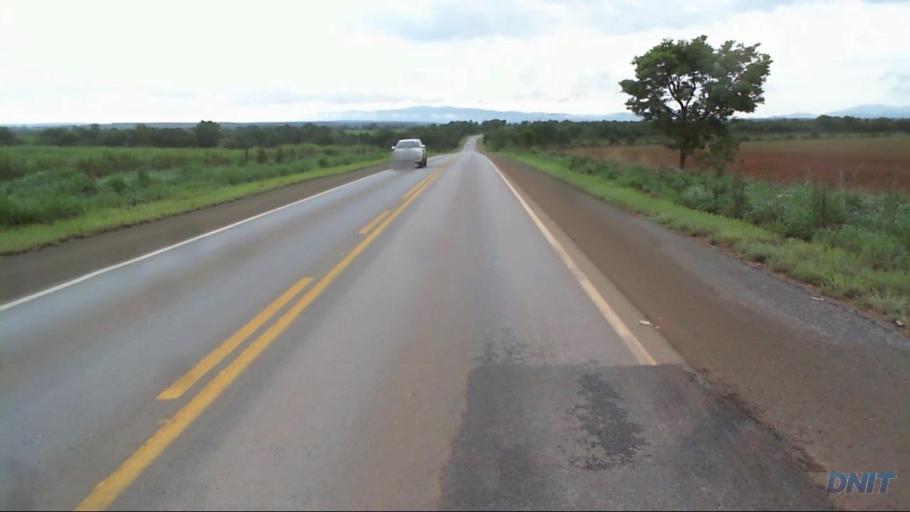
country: BR
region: Goias
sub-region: Uruacu
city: Uruacu
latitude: -14.7228
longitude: -49.0985
